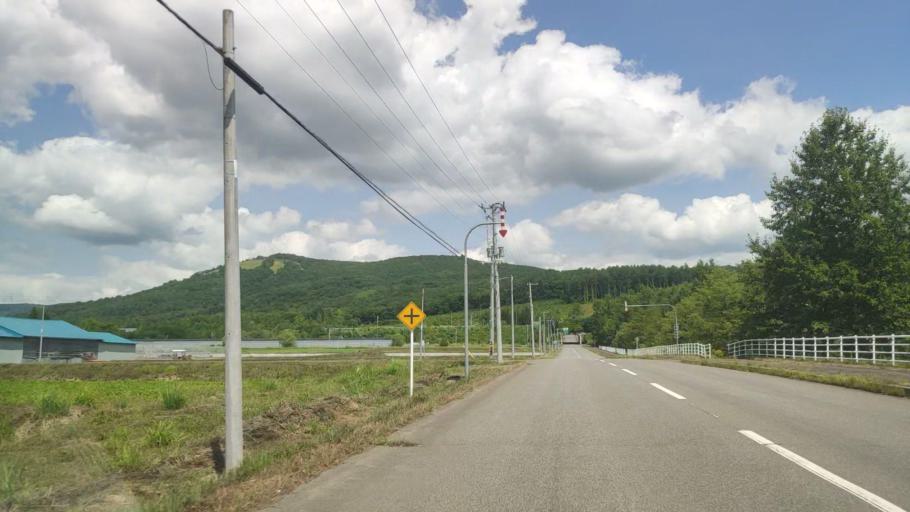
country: JP
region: Hokkaido
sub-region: Asahikawa-shi
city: Asahikawa
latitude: 43.9154
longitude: 142.4976
